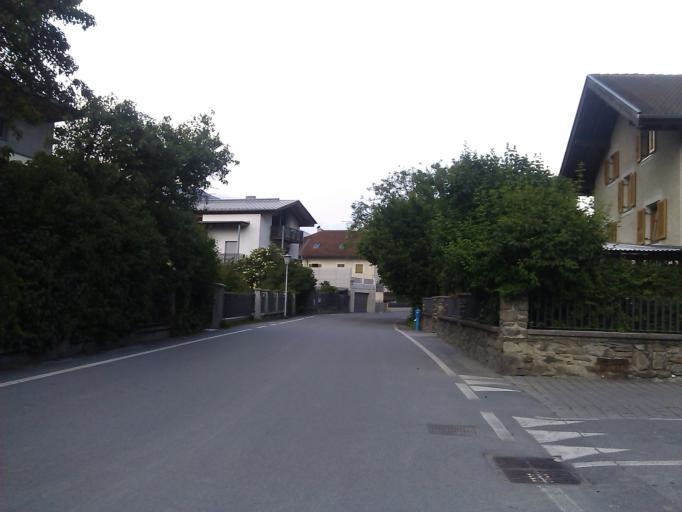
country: IT
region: Trentino-Alto Adige
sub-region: Bolzano
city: Lasa
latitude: 46.6154
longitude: 10.6966
